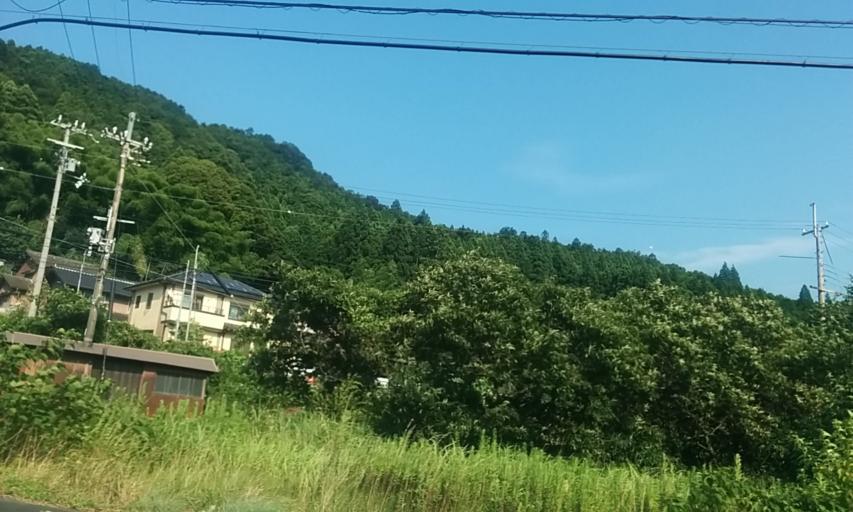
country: JP
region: Kyoto
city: Maizuru
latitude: 35.4791
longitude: 135.2835
